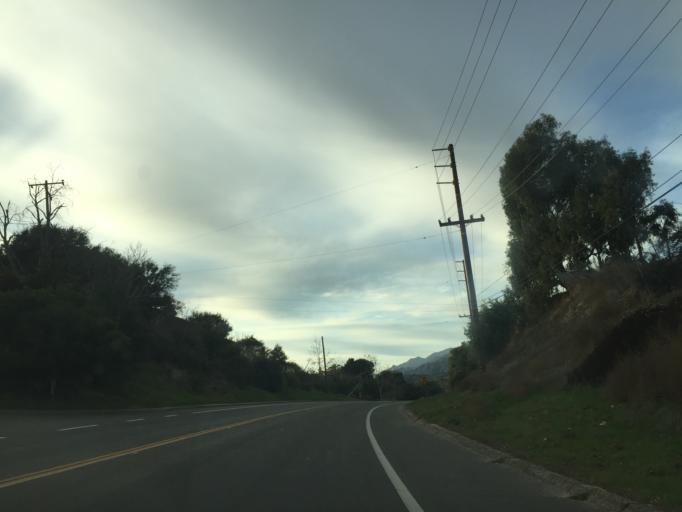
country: US
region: California
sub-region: Santa Barbara County
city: Goleta
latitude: 34.4517
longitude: -119.8039
